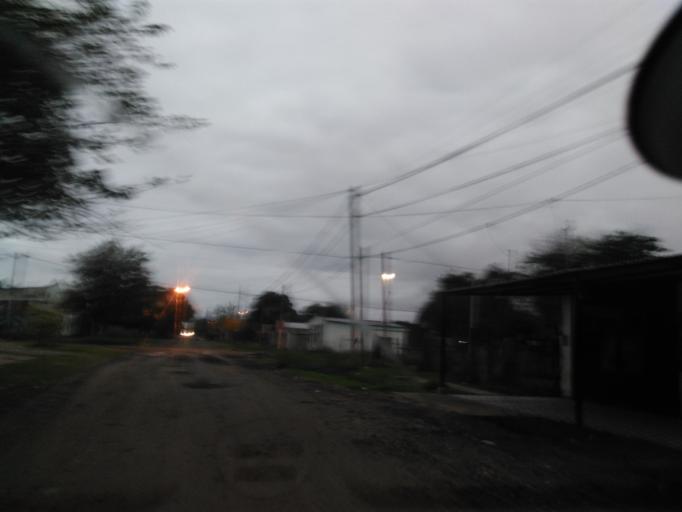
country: AR
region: Chaco
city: Resistencia
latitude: -27.4762
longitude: -58.9898
